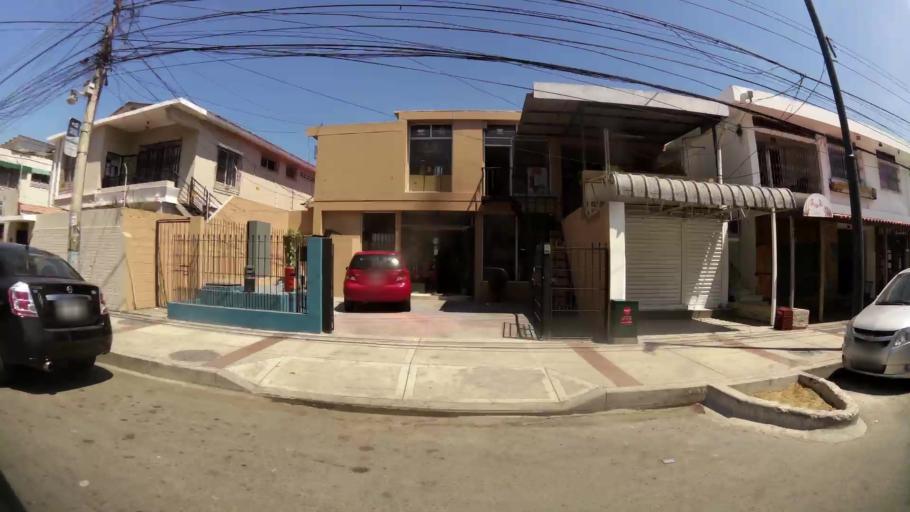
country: EC
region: Guayas
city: Guayaquil
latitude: -2.1653
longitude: -79.9118
